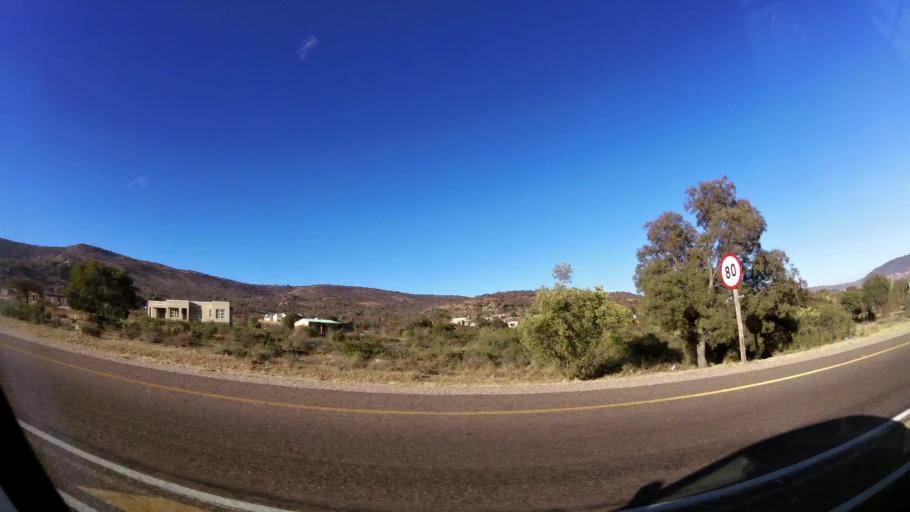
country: ZA
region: Limpopo
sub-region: Capricorn District Municipality
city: Mankoeng
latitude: -23.9433
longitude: 29.8143
